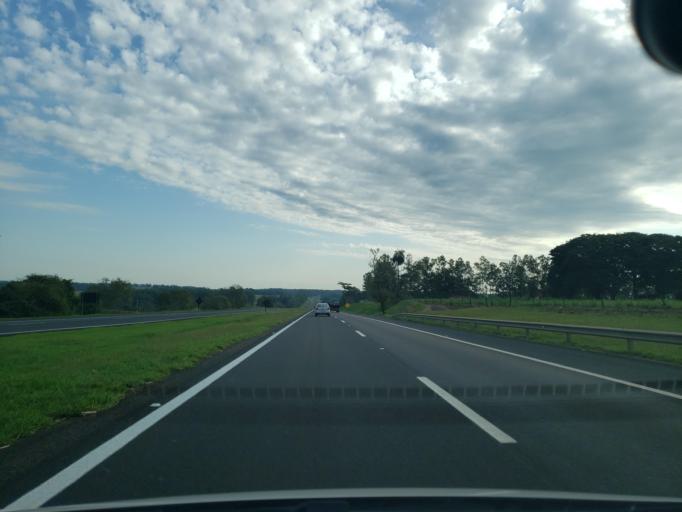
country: BR
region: Sao Paulo
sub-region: Guararapes
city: Guararapes
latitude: -21.2091
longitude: -50.6648
